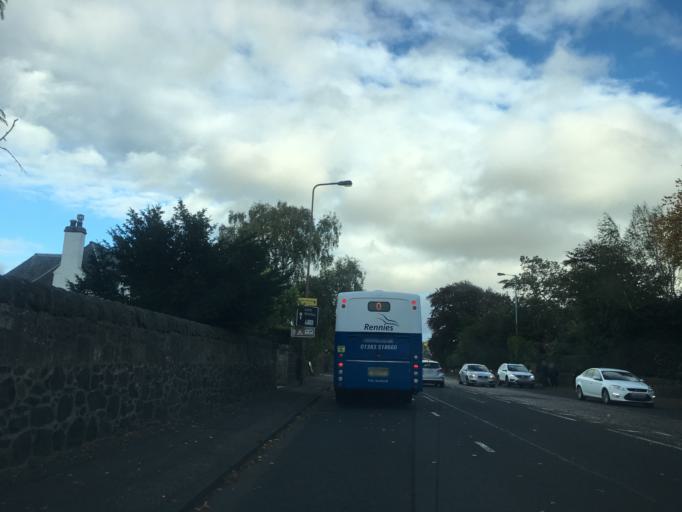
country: GB
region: Scotland
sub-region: Edinburgh
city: Currie
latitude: 55.9611
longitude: -3.3087
